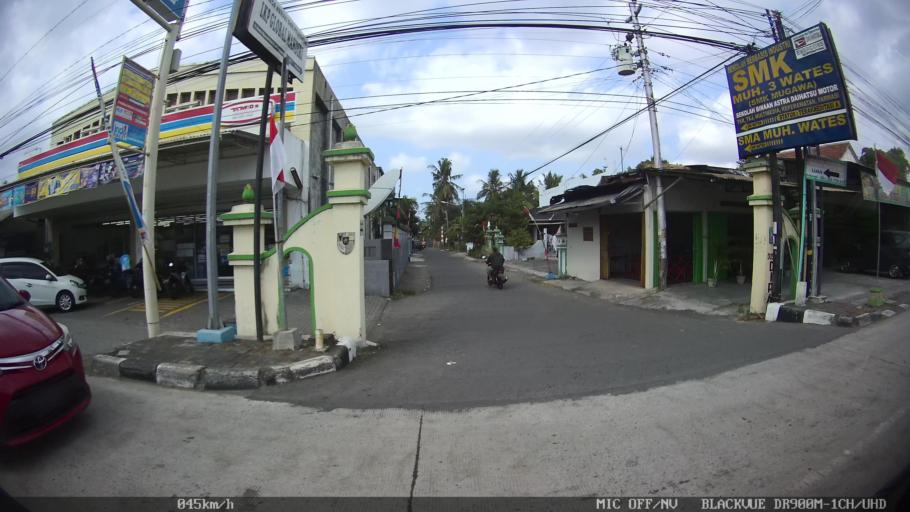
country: ID
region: Daerah Istimewa Yogyakarta
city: Srandakan
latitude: -7.8652
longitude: 110.1532
